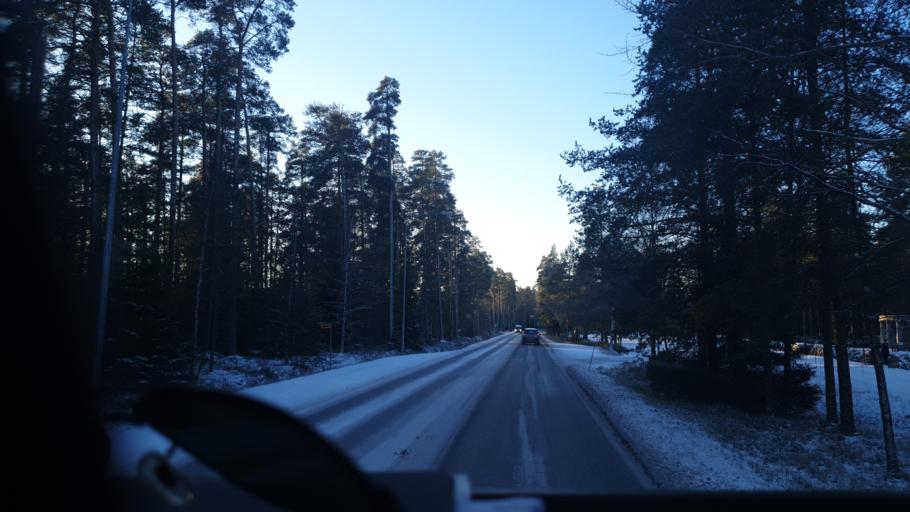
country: FI
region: Central Ostrobothnia
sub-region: Kokkola
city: Kokkola
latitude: 63.8287
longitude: 23.1025
